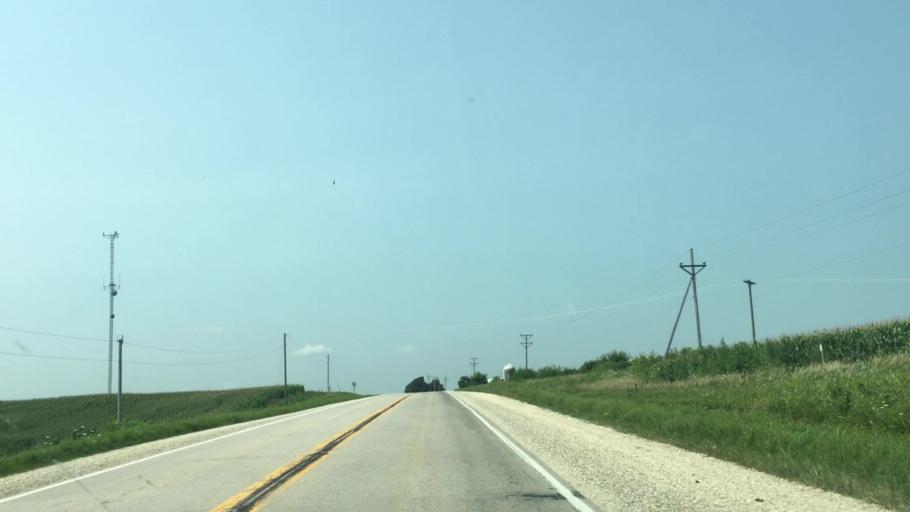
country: US
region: Iowa
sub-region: Fayette County
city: West Union
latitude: 43.0887
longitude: -91.8518
